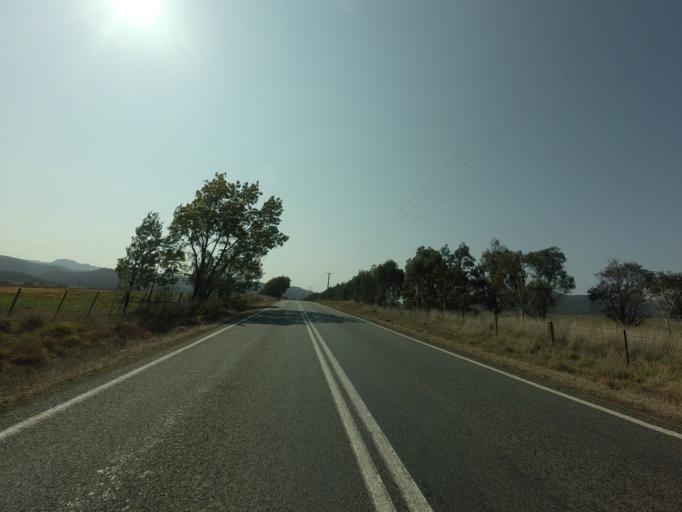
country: AU
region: Tasmania
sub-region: Northern Midlands
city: Evandale
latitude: -41.7941
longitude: 147.7091
